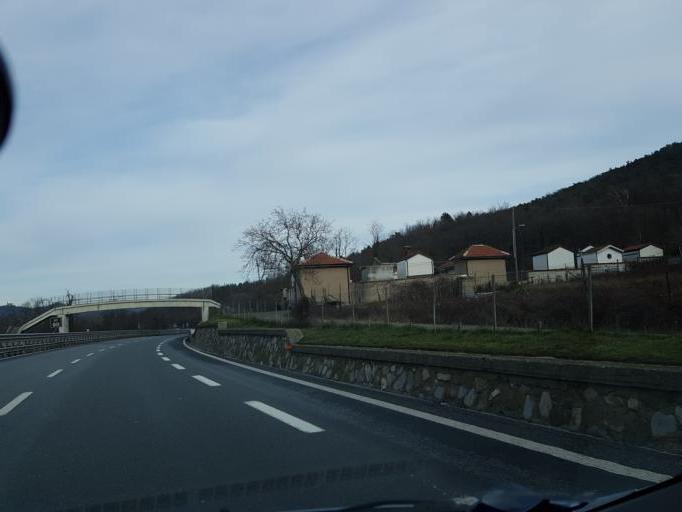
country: IT
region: Piedmont
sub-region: Provincia di Alessandria
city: Arquata Scrivia
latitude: 44.6738
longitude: 8.9053
